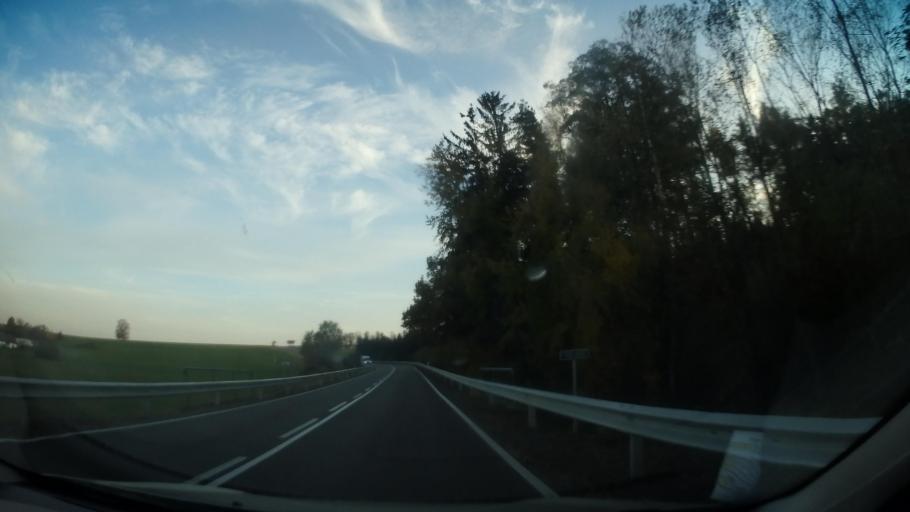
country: CZ
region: Central Bohemia
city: Vlasim
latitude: 49.6790
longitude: 14.9488
